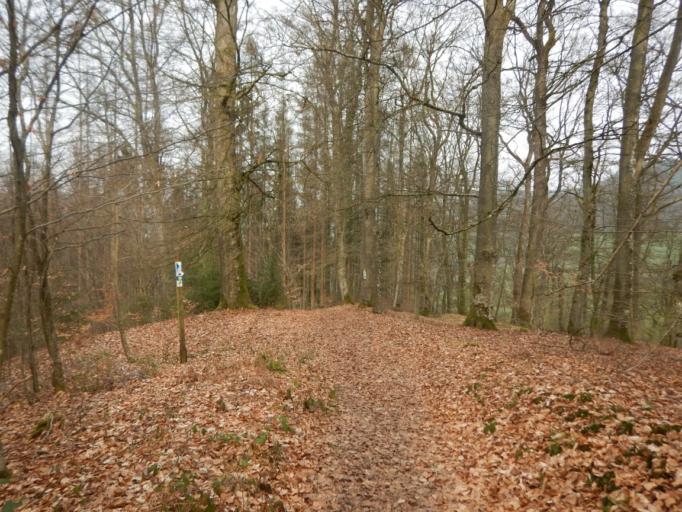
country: LU
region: Grevenmacher
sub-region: Canton d'Echternach
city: Berdorf
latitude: 49.8331
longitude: 6.3266
